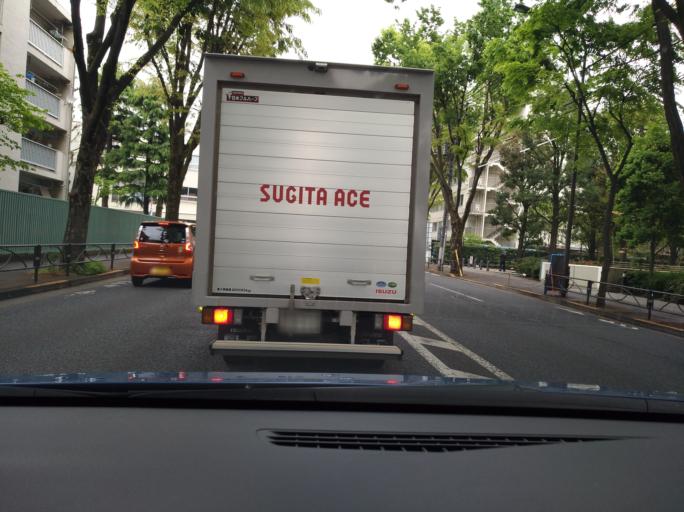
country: JP
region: Tokyo
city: Mitaka-shi
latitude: 35.6723
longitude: 139.6036
